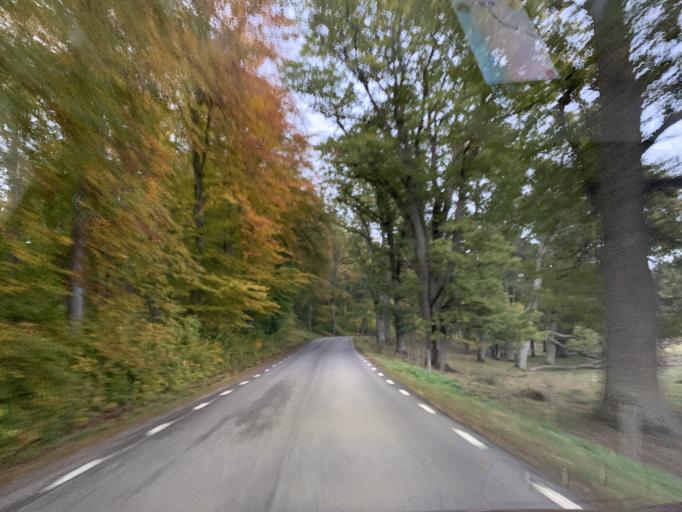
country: SE
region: Stockholm
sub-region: Nynashamns Kommun
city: Osmo
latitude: 58.9623
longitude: 17.7674
